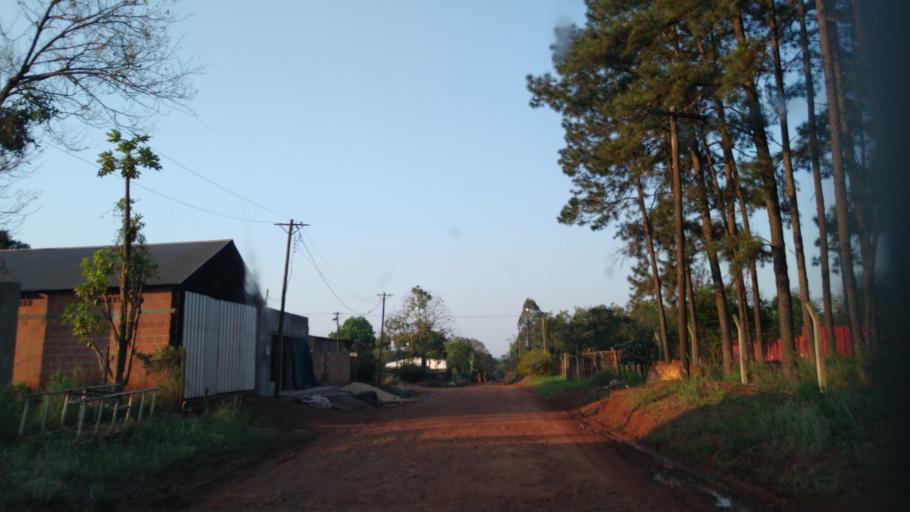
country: AR
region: Misiones
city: Jardin America
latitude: -27.0705
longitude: -55.2681
